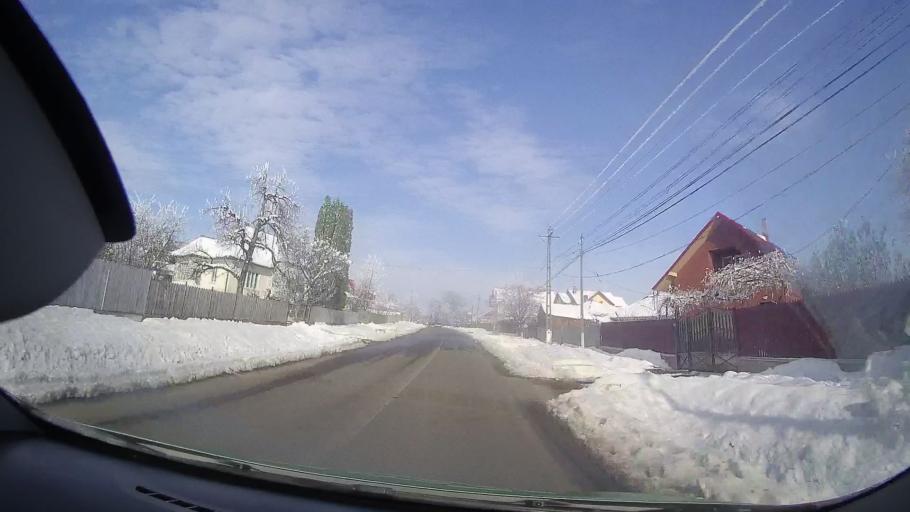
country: RO
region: Iasi
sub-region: Comuna Cristesti
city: Cristesti
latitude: 47.2559
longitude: 26.5749
